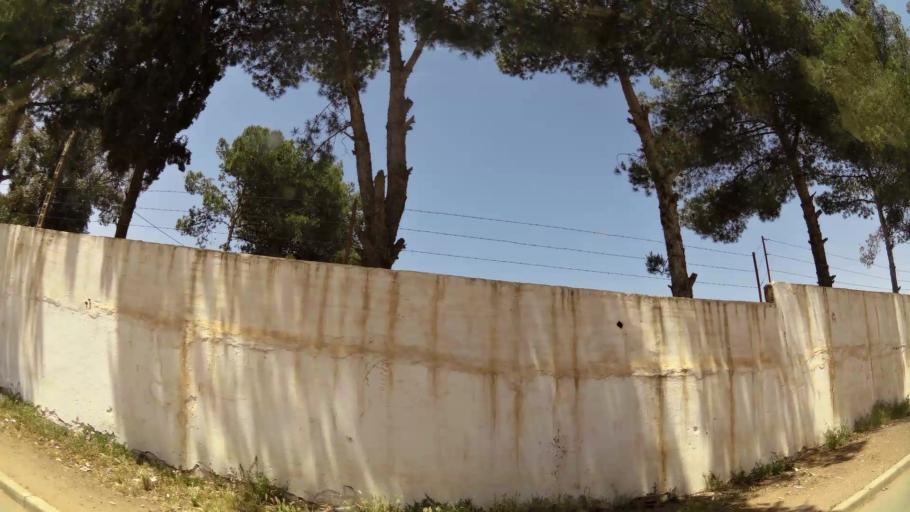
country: MA
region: Rabat-Sale-Zemmour-Zaer
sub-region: Khemisset
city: Khemisset
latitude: 33.8310
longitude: -6.0908
